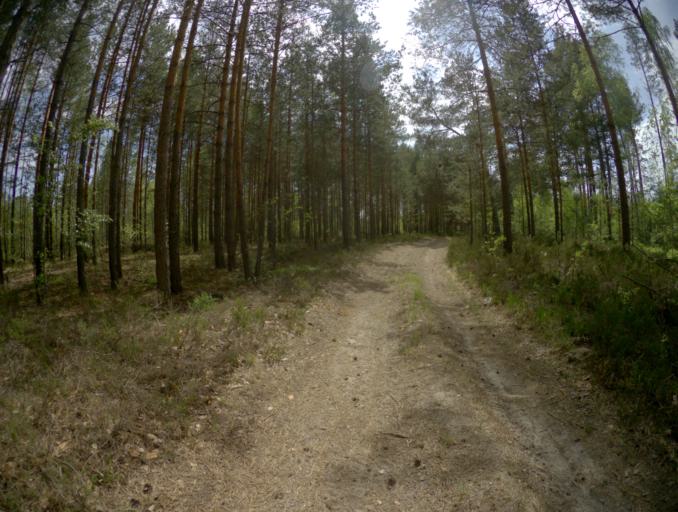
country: RU
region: Vladimir
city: Ivanishchi
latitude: 55.6881
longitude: 40.4038
